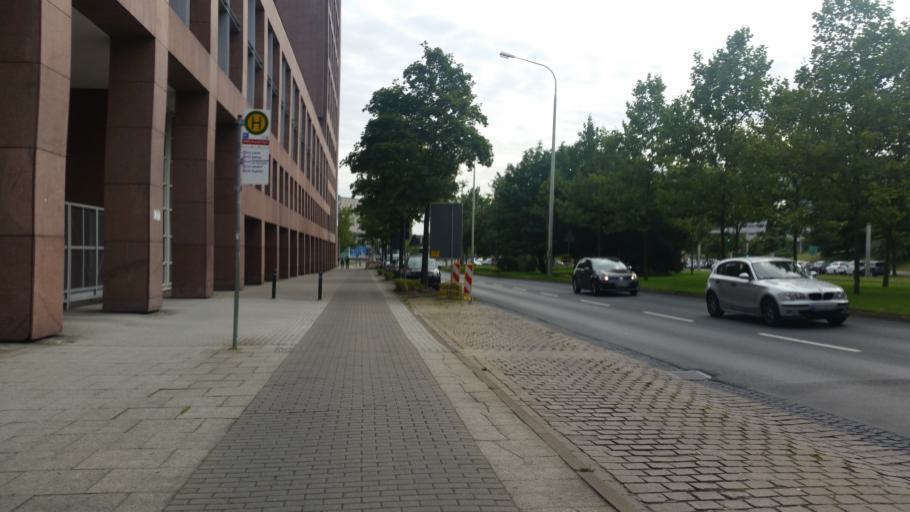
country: DE
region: Lower Saxony
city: Braunschweig
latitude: 52.2556
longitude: 10.5401
